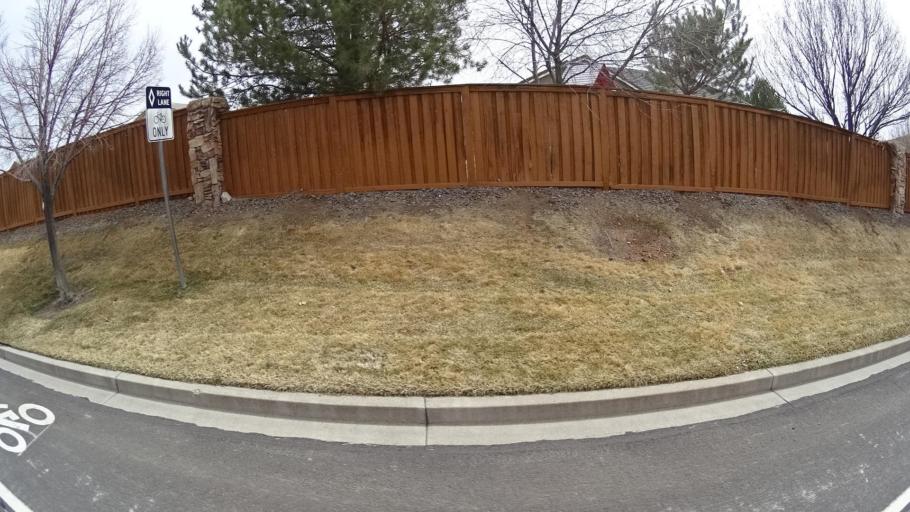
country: US
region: Nevada
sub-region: Washoe County
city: Spanish Springs
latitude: 39.6322
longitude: -119.6804
